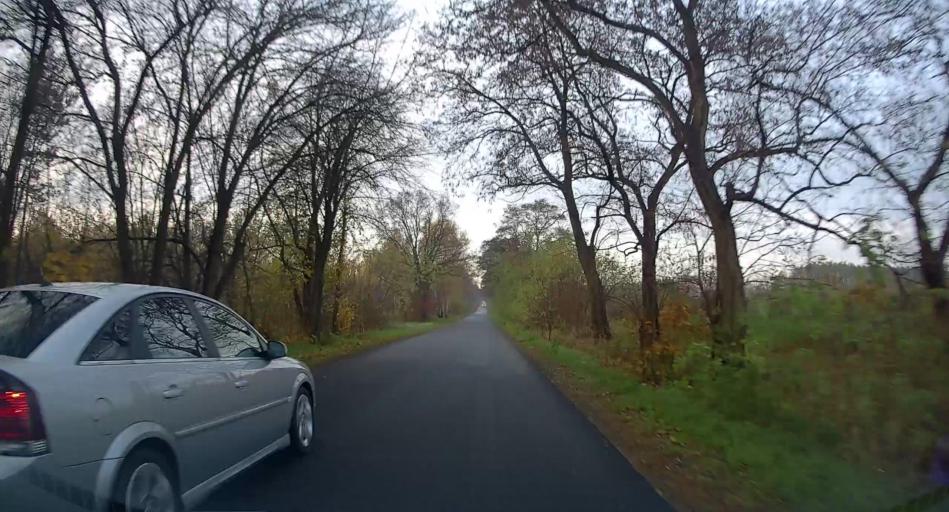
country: PL
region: Masovian Voivodeship
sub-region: Powiat zyrardowski
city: Puszcza Marianska
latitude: 51.9350
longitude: 20.3647
